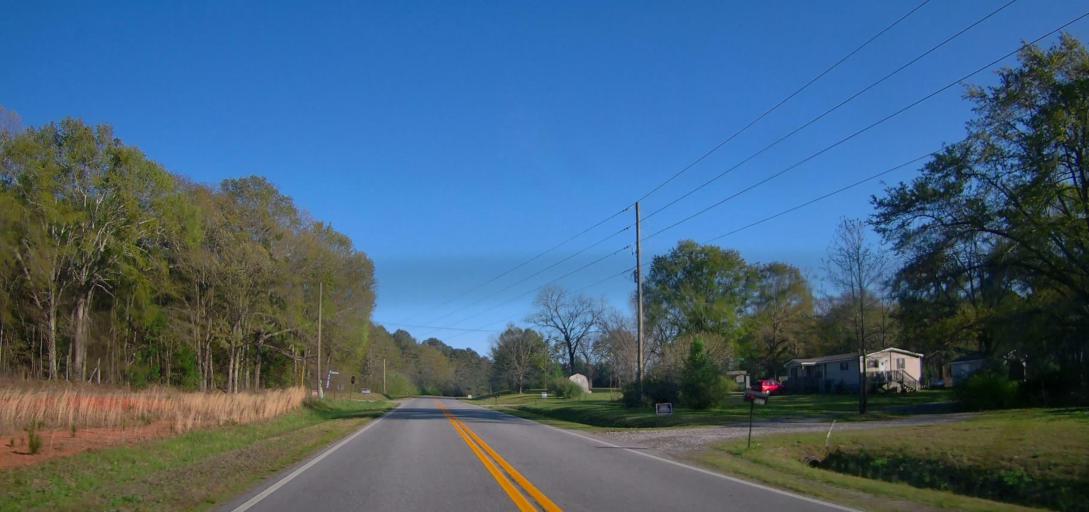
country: US
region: Georgia
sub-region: Butts County
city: Jackson
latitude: 33.3269
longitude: -83.9043
